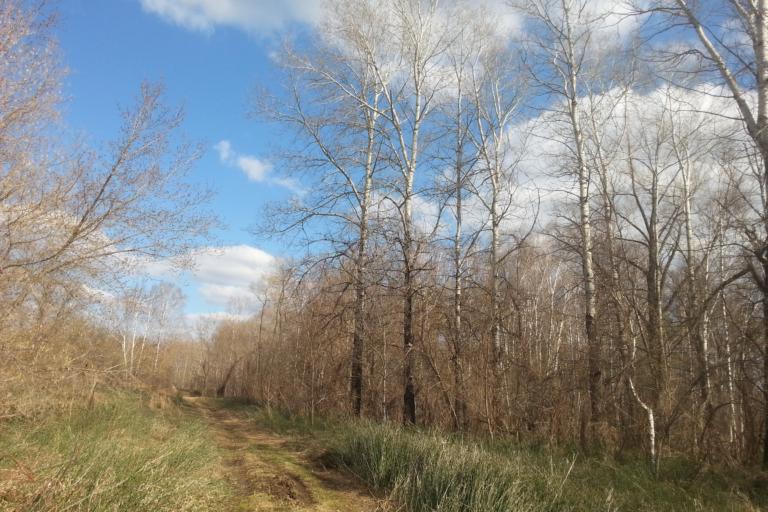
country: RU
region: Altai Krai
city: Sannikovo
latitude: 53.3330
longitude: 84.0149
